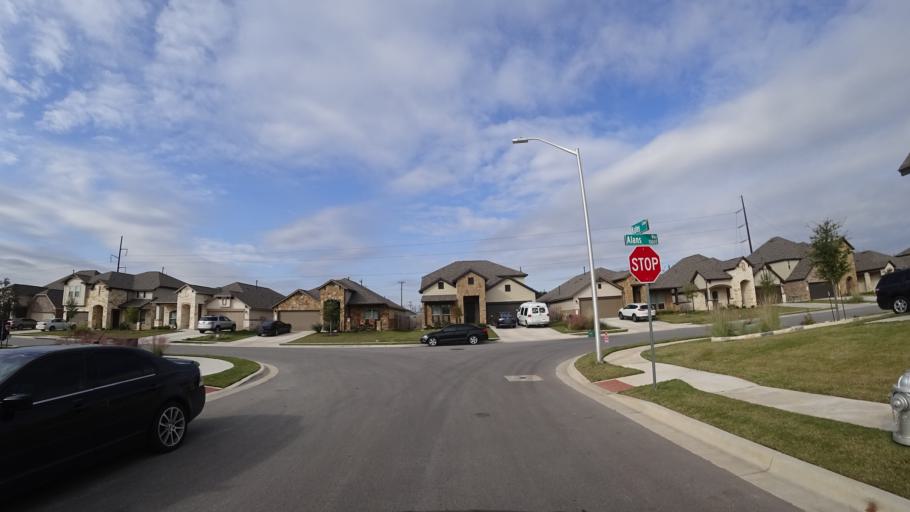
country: US
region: Texas
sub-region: Travis County
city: Manchaca
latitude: 30.1339
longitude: -97.8490
